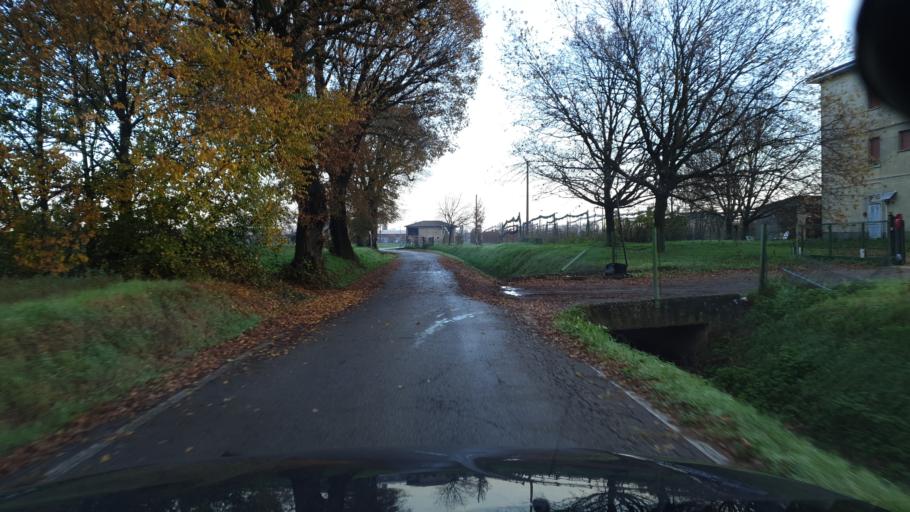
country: IT
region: Emilia-Romagna
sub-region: Provincia di Bologna
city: Crespellano
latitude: 44.5199
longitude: 11.1430
